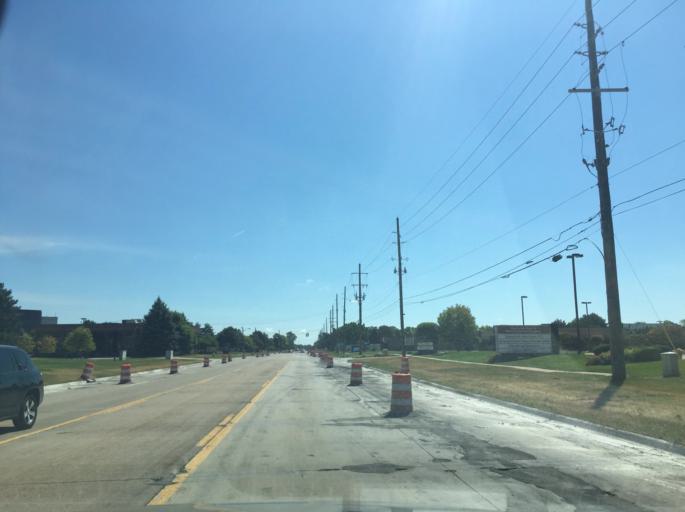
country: US
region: Michigan
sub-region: Macomb County
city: Clinton
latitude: 42.6126
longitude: -82.9652
